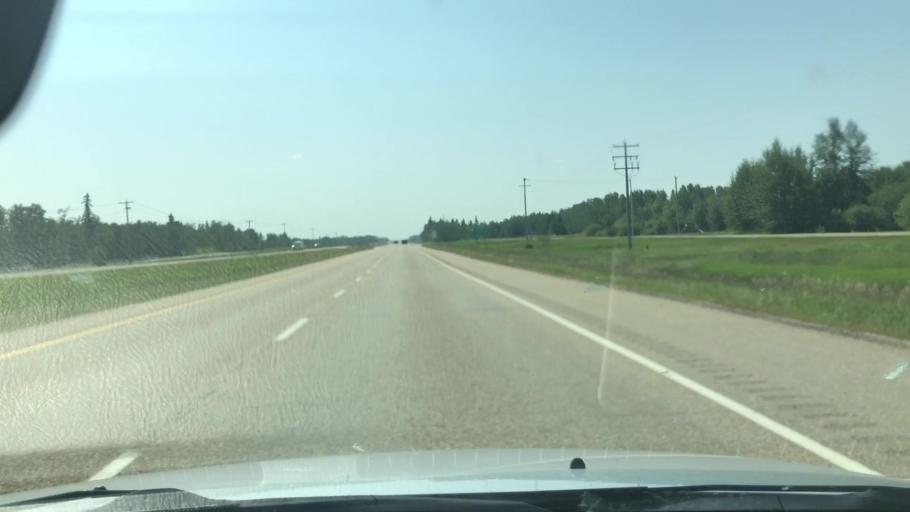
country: CA
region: Alberta
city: Devon
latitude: 53.4388
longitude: -113.7630
